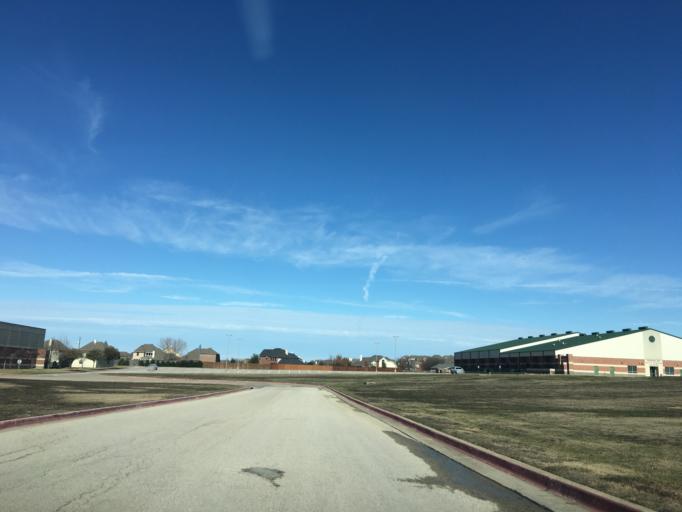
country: US
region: Texas
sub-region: Collin County
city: Prosper
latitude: 33.2415
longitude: -96.7982
